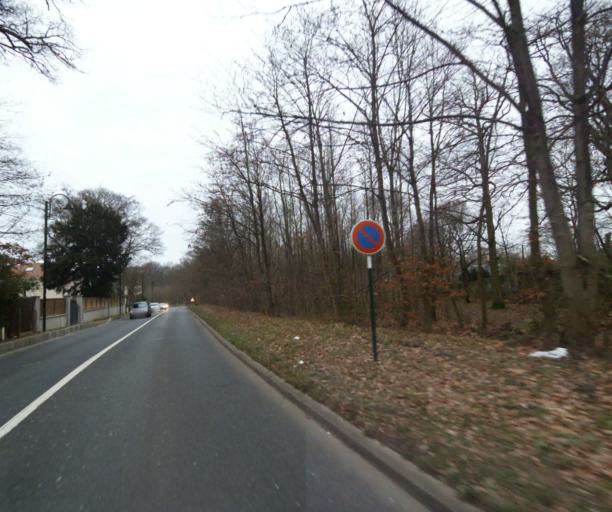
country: FR
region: Ile-de-France
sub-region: Departement des Yvelines
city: La Celle-Saint-Cloud
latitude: 48.8407
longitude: 2.1458
